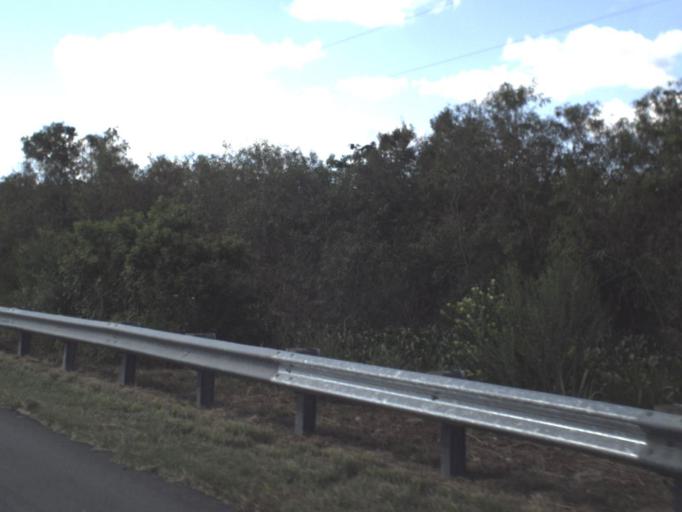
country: US
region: Florida
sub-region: Miami-Dade County
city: Kendall West
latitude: 25.8590
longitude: -81.0538
